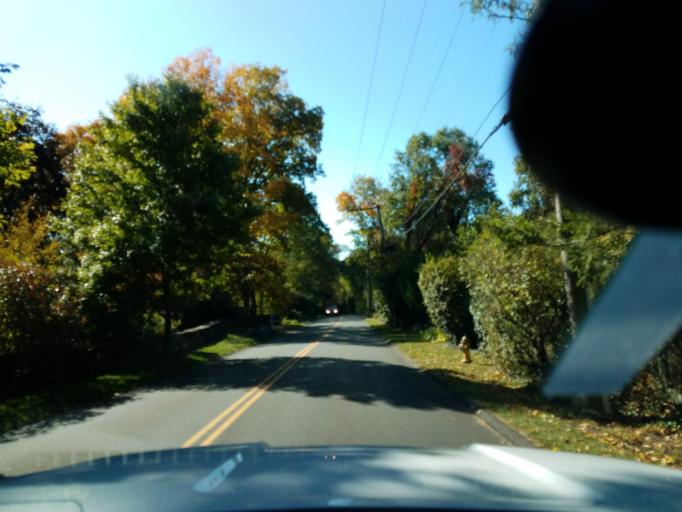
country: US
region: Connecticut
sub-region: Fairfield County
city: Cos Cob
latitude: 41.0456
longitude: -73.6154
